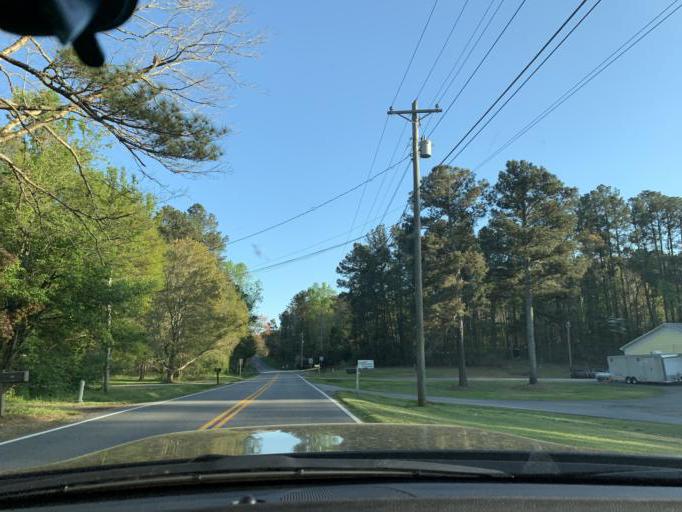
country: US
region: Georgia
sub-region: Forsyth County
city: Cumming
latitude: 34.2474
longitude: -84.1911
